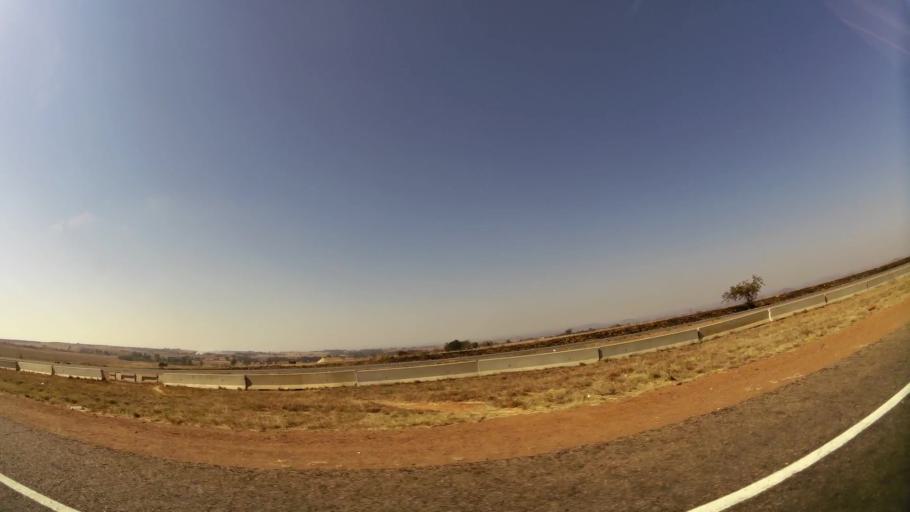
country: ZA
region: Gauteng
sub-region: City of Tshwane Metropolitan Municipality
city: Mabopane
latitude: -25.5428
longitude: 28.1119
